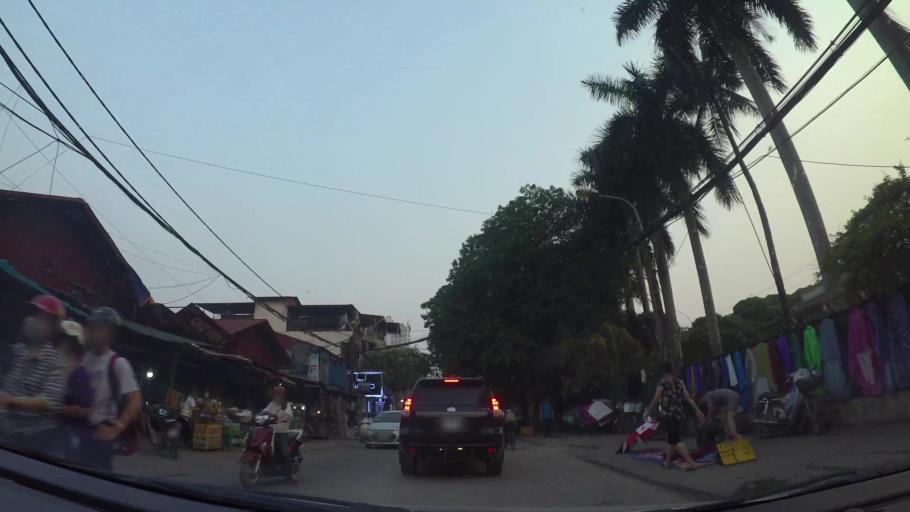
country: VN
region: Ha Noi
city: Cau Giay
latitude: 21.0495
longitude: 105.7899
